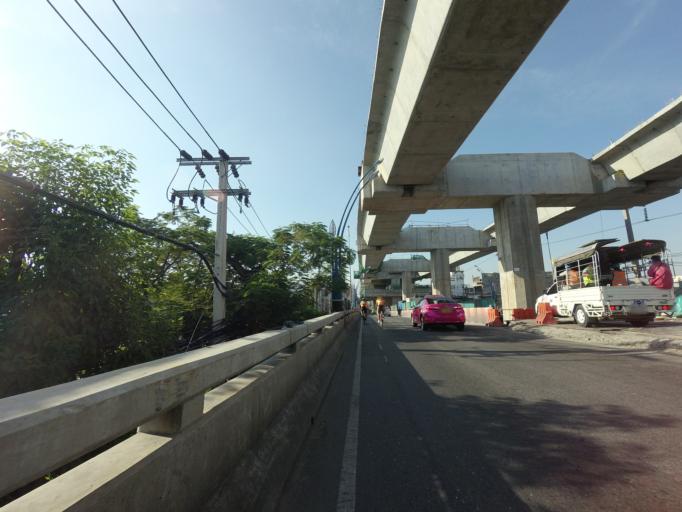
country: TH
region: Samut Prakan
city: Samut Prakan
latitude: 13.6475
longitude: 100.5963
